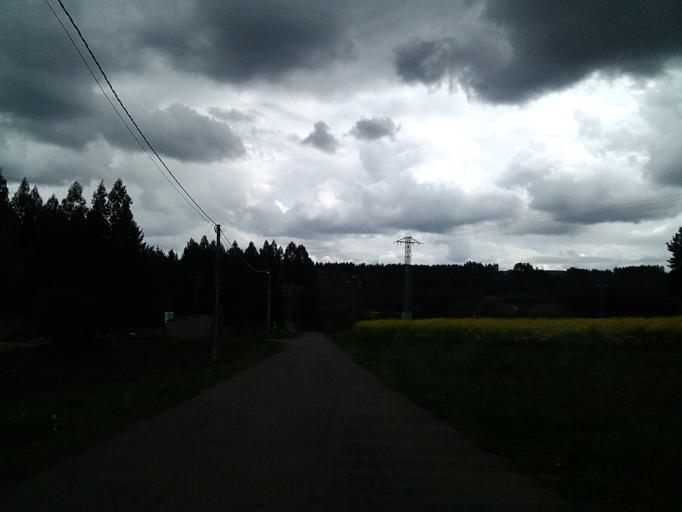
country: ES
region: Galicia
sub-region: Provincia de Lugo
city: Begonte
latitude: 43.1387
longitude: -7.7709
